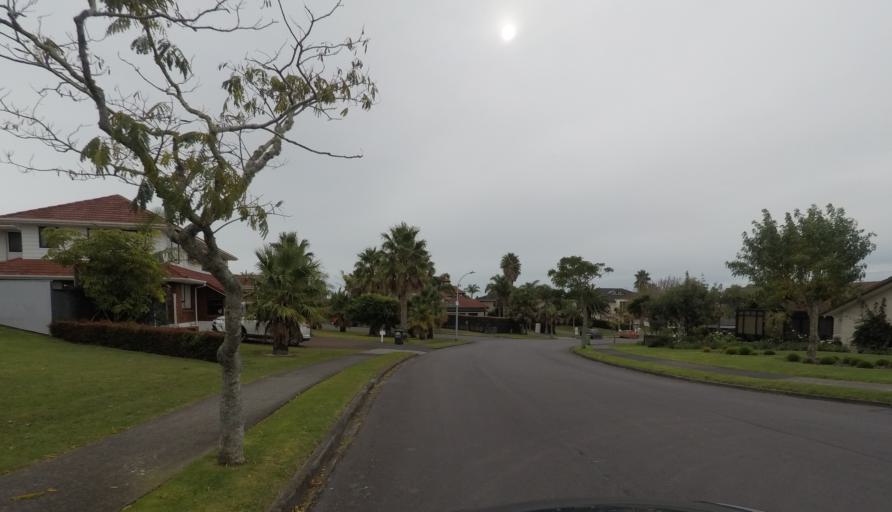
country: NZ
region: Auckland
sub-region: Auckland
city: Pakuranga
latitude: -36.8958
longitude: 174.9481
